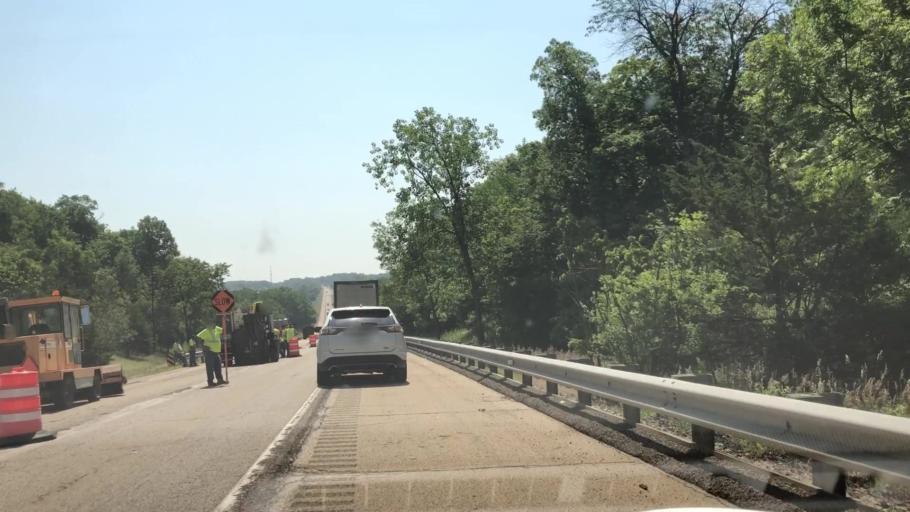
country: US
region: Illinois
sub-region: Woodford County
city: Eureka
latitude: 40.6161
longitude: -89.2575
